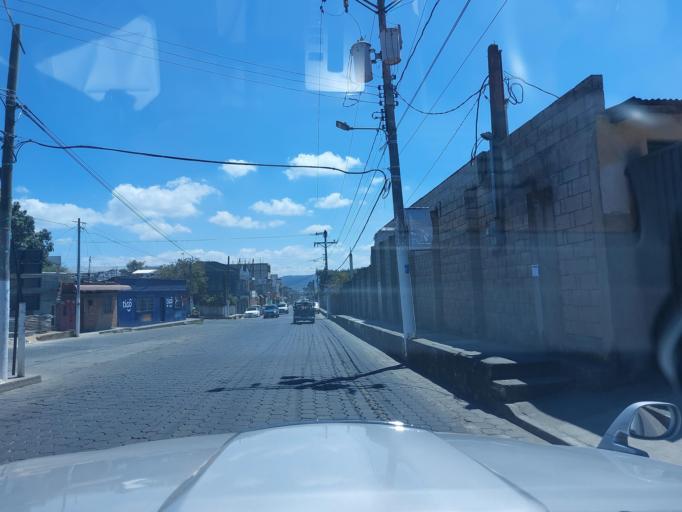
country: GT
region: Chimaltenango
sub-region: Municipio de Chimaltenango
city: Chimaltenango
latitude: 14.6620
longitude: -90.8269
